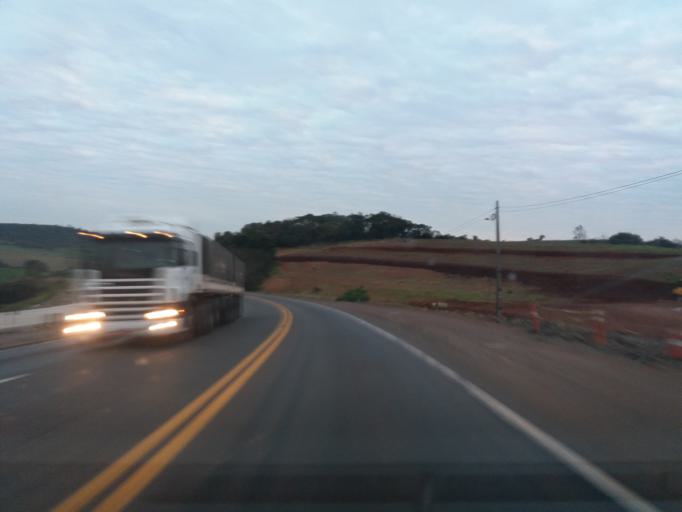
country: BR
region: Parana
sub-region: Realeza
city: Realeza
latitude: -25.3737
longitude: -53.5748
